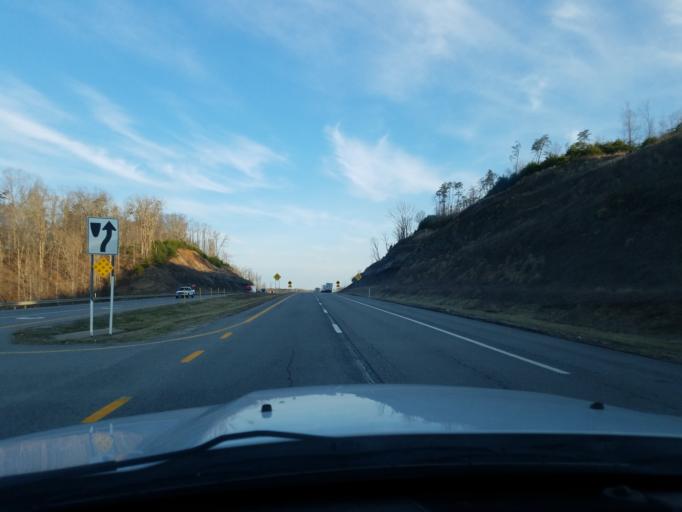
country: US
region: West Virginia
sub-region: Putnam County
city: Buffalo
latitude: 38.5714
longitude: -82.0143
